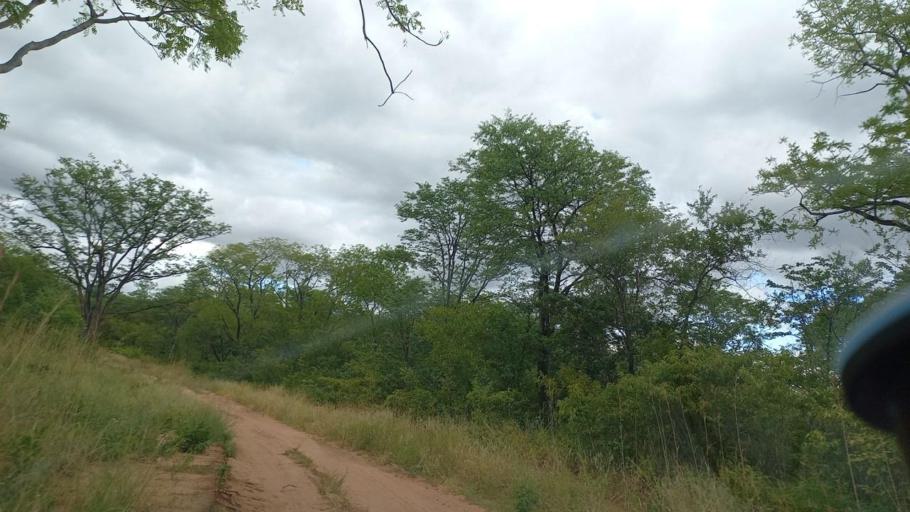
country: ZM
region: Lusaka
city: Luangwa
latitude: -15.5710
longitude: 30.3165
